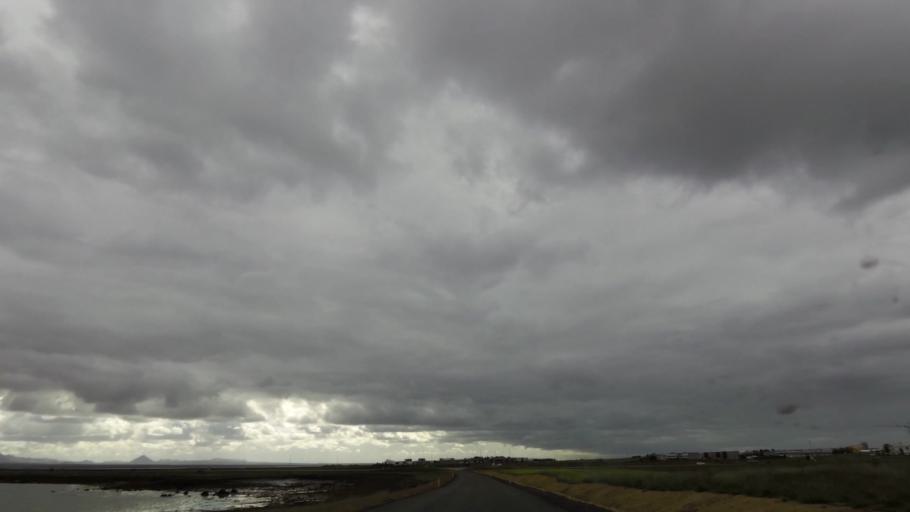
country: IS
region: Capital Region
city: Alftanes
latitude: 64.1042
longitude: -22.0032
